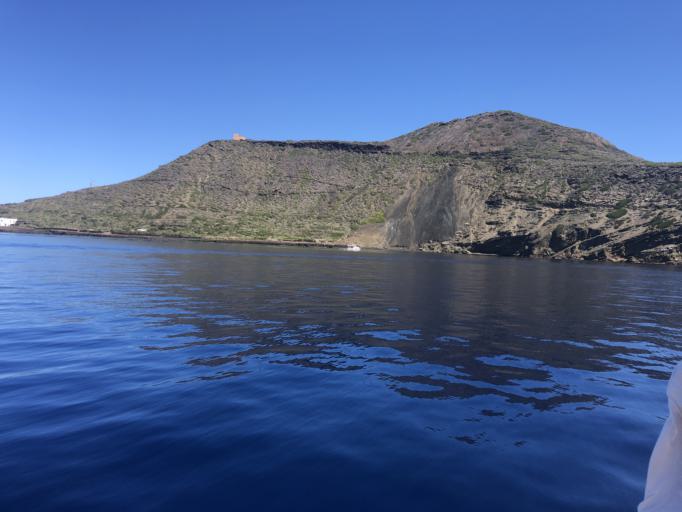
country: IT
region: Sicily
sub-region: Agrigento
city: Lampedusa
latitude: 35.8524
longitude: 12.8723
